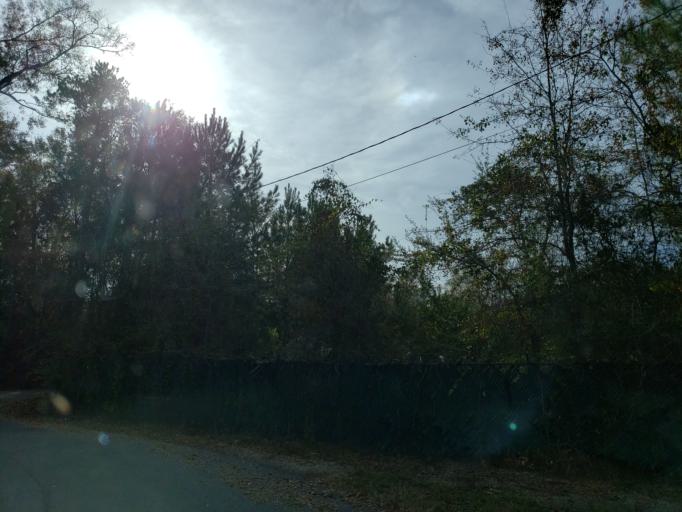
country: US
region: Mississippi
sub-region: Forrest County
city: Hattiesburg
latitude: 31.3345
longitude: -89.3089
